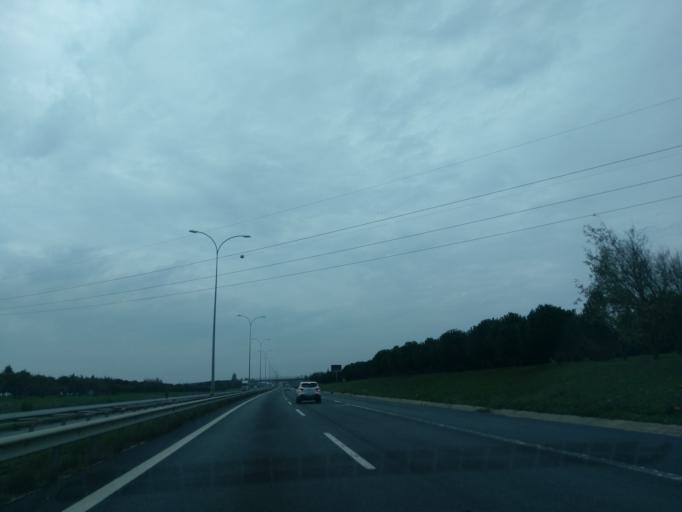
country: TR
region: Istanbul
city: Silivri
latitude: 41.1182
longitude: 28.2045
